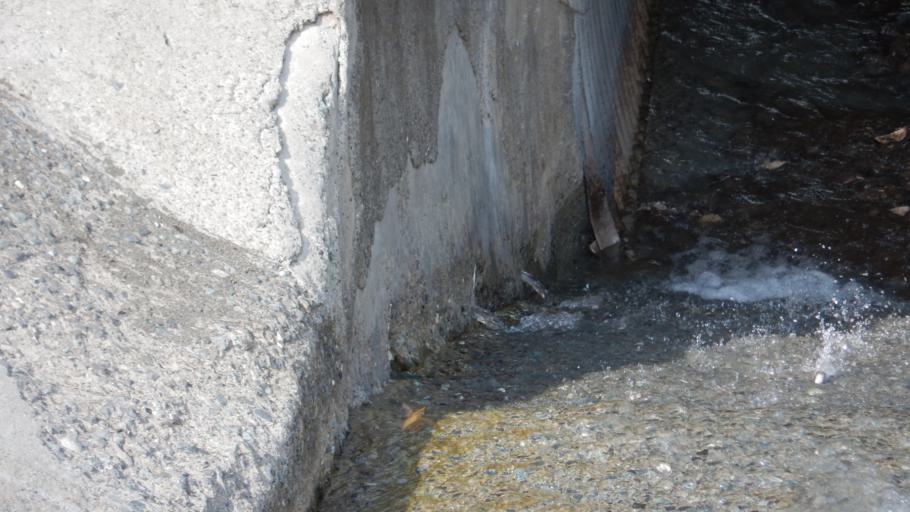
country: PG
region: Eastern Highlands
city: Kainantu
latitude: -6.3908
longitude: 146.4217
